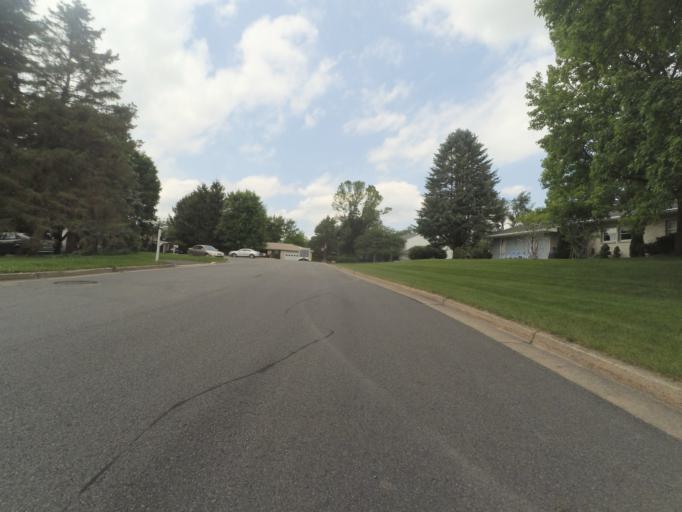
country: US
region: Pennsylvania
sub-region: Centre County
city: State College
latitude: 40.7780
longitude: -77.8599
